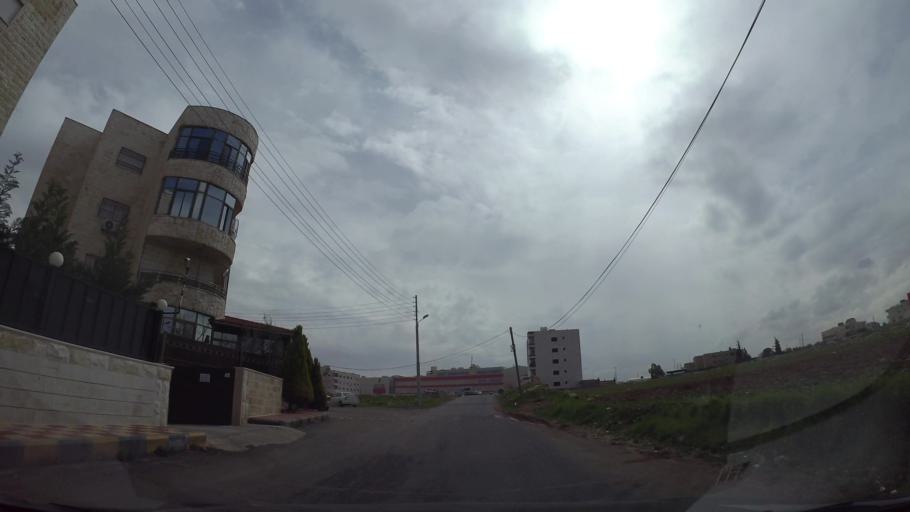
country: JO
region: Amman
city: Amman
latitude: 31.9956
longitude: 35.9340
